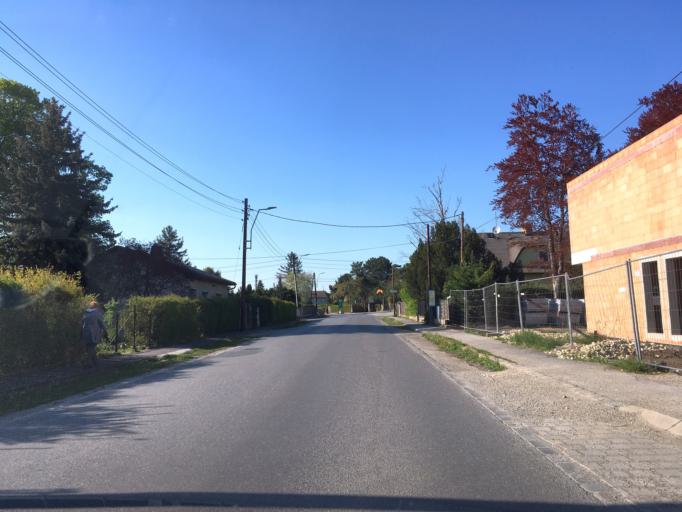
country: AT
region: Lower Austria
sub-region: Politischer Bezirk Ganserndorf
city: Strasshof an der Nordbahn
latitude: 48.3248
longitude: 16.6817
